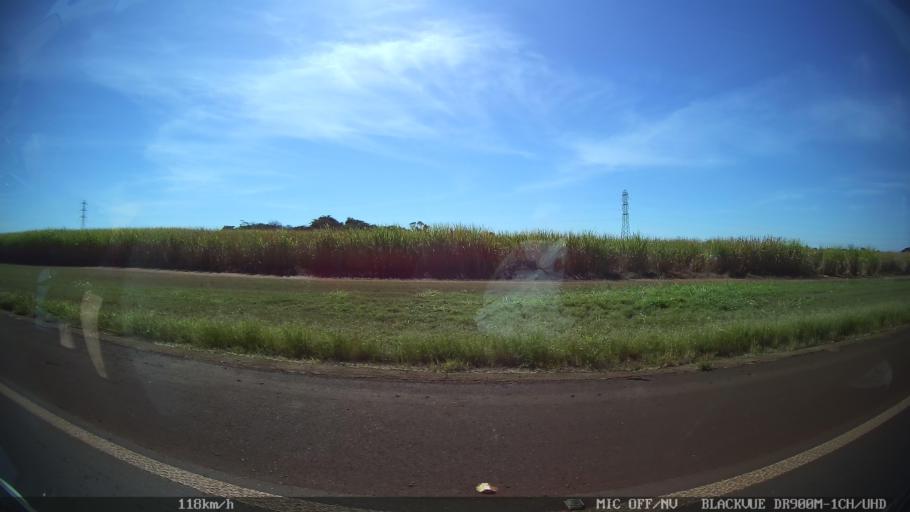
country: BR
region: Sao Paulo
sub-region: Guaira
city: Guaira
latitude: -20.4452
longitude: -48.2285
